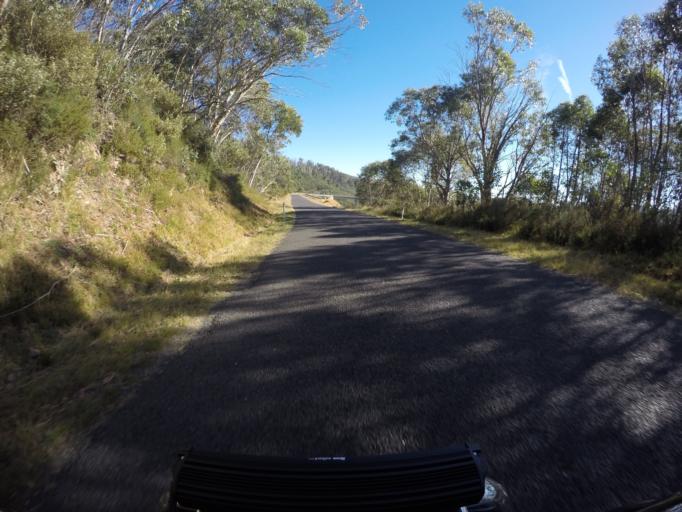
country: AU
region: New South Wales
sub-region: Snowy River
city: Jindabyne
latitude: -36.0531
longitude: 148.2729
